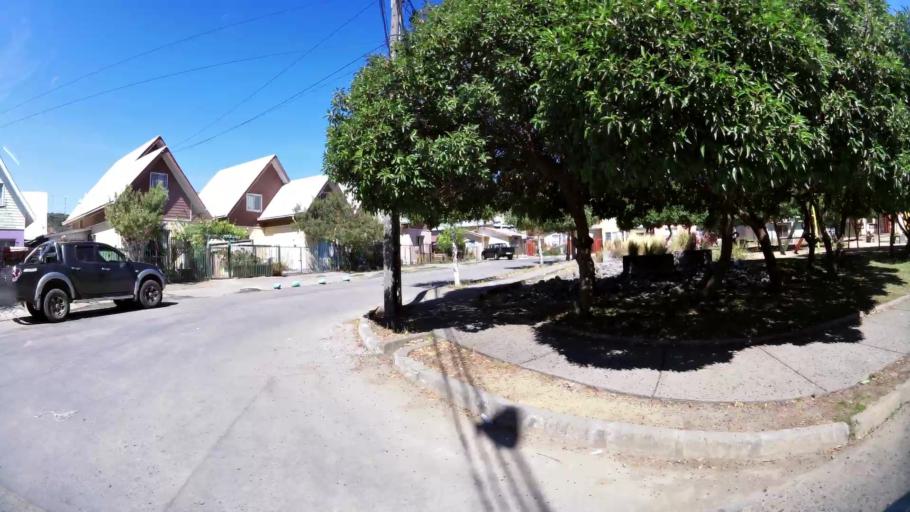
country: CL
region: Biobio
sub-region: Provincia de Concepcion
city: Penco
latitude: -36.7277
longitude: -72.9821
